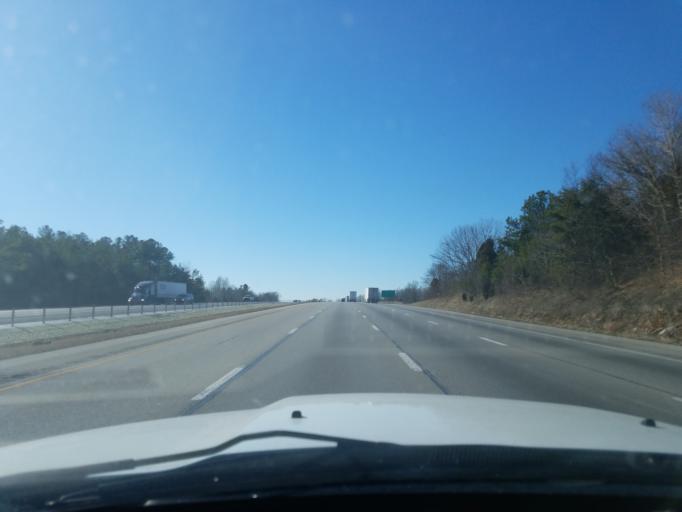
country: US
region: Kentucky
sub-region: Hardin County
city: Elizabethtown
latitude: 37.7327
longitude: -85.8128
